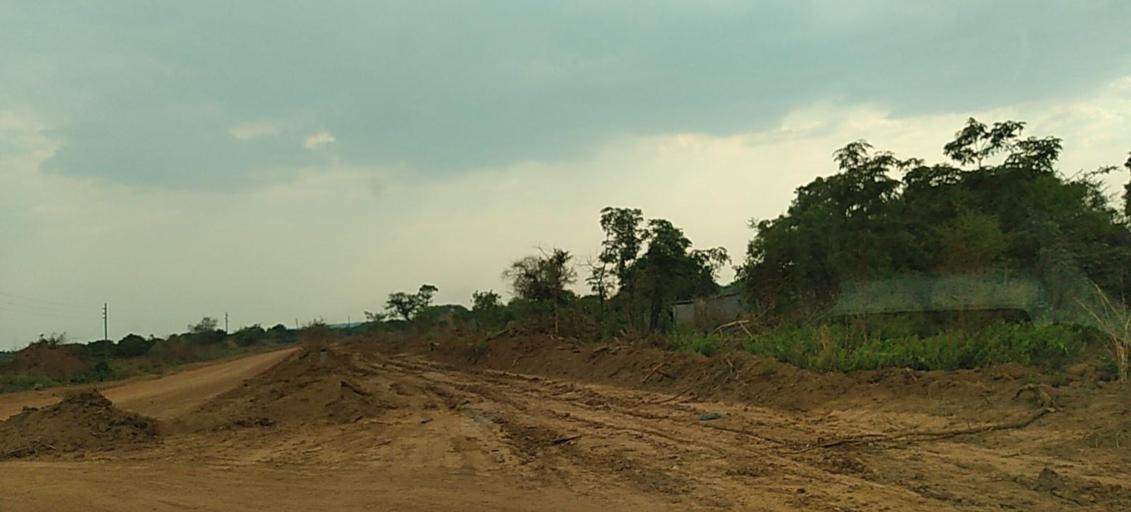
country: ZM
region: Copperbelt
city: Kalulushi
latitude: -12.9262
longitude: 27.9397
